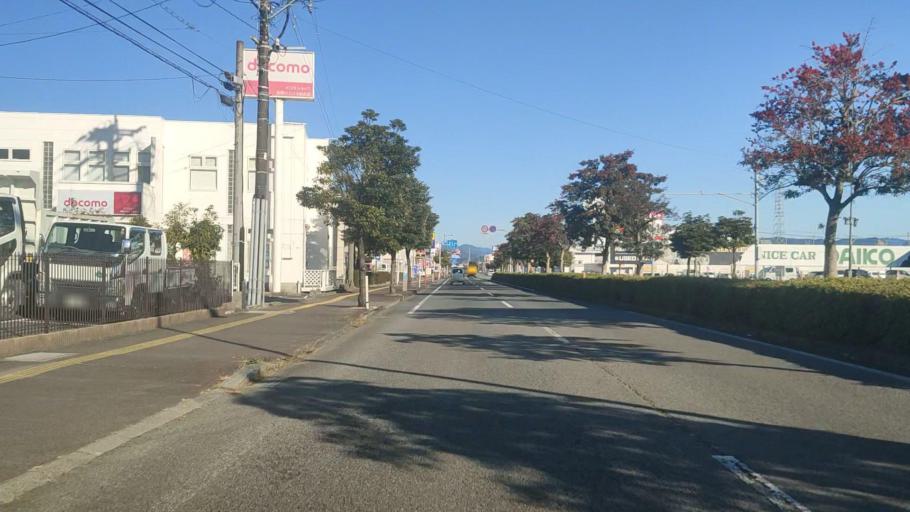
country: JP
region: Miyazaki
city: Nobeoka
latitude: 32.5699
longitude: 131.6836
